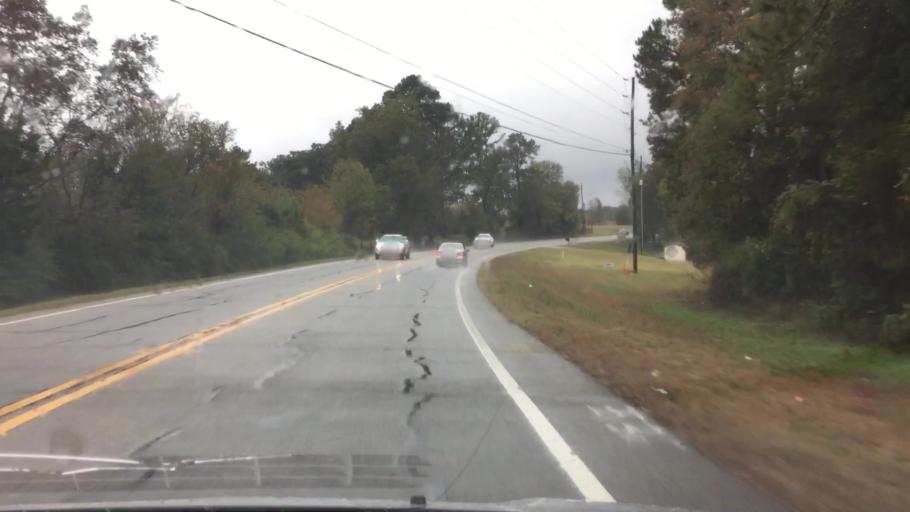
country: US
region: Georgia
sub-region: Henry County
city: Stockbridge
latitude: 33.5696
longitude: -84.1458
